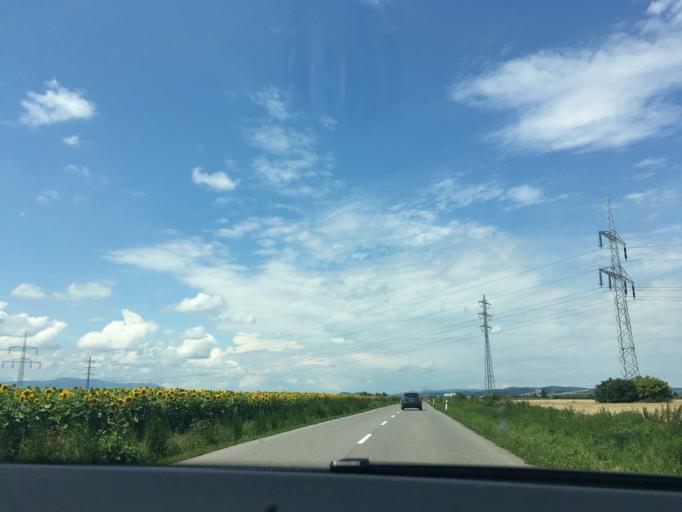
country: SK
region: Presovsky
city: Vranov nad Topl'ou
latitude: 48.8272
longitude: 21.7231
